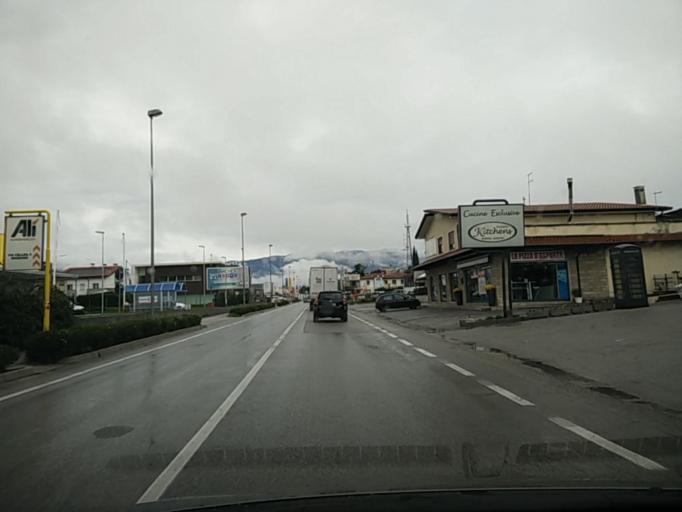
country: IT
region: Veneto
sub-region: Provincia di Vicenza
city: San Zeno-San Giuseppe
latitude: 45.7318
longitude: 11.7609
